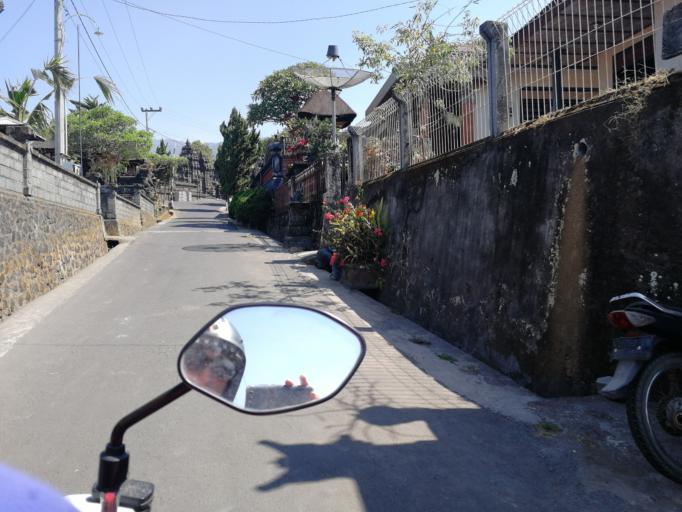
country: ID
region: Bali
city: Banjar Kedisan
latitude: -8.1526
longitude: 115.3082
